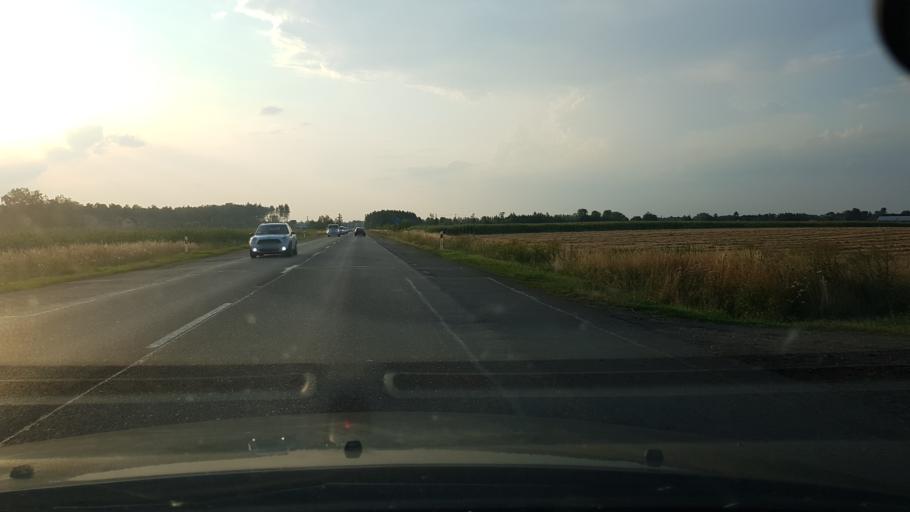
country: PL
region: Masovian Voivodeship
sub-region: Powiat plonski
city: Plonsk
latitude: 52.6907
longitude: 20.3534
